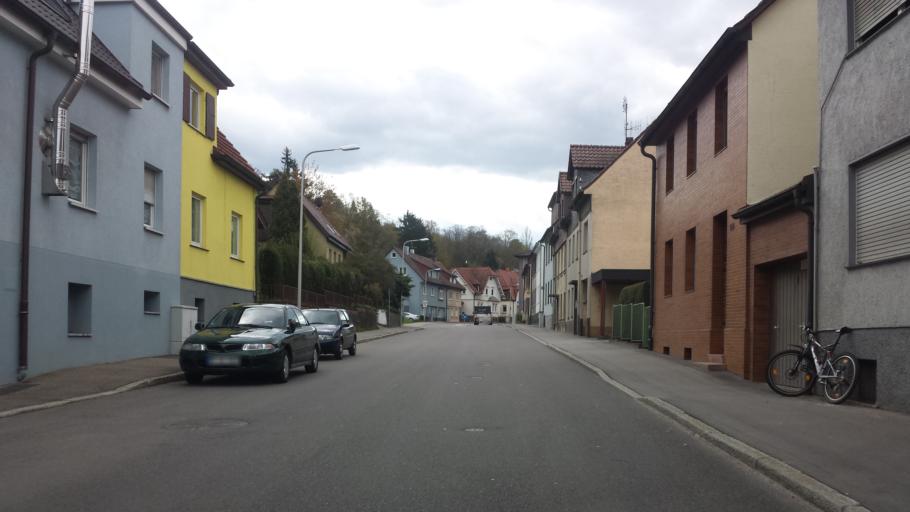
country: DE
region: Baden-Wuerttemberg
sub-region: Karlsruhe Region
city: Niefern-Oschelbronn
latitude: 48.9127
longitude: 8.7890
